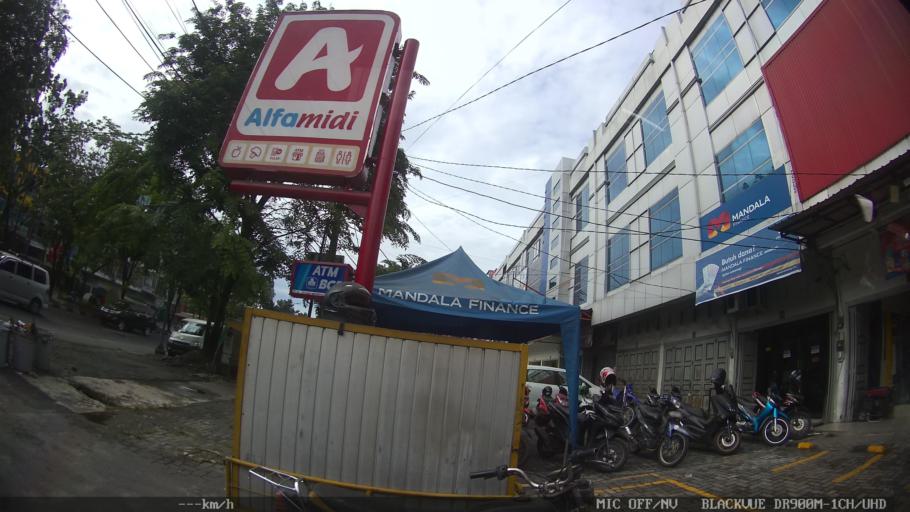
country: ID
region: North Sumatra
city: Sunggal
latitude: 3.5988
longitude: 98.6269
